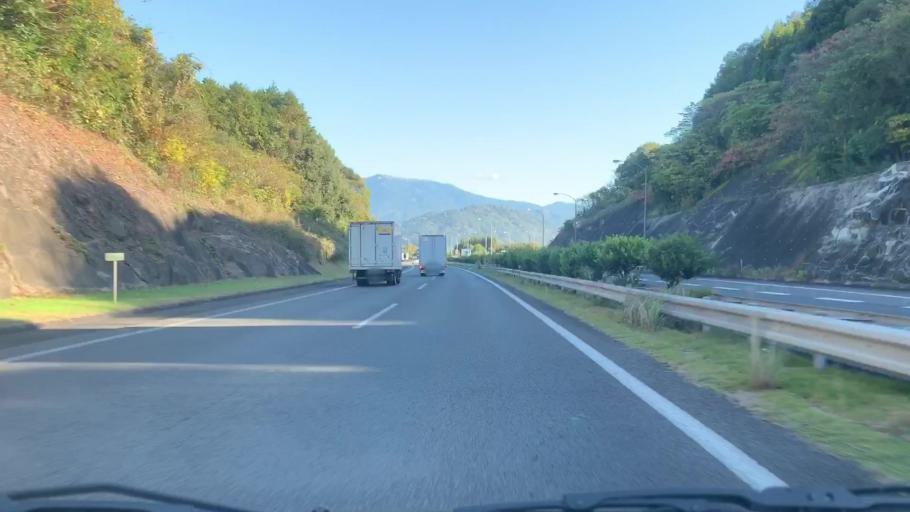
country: JP
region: Saga Prefecture
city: Takeocho-takeo
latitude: 33.2505
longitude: 130.0763
